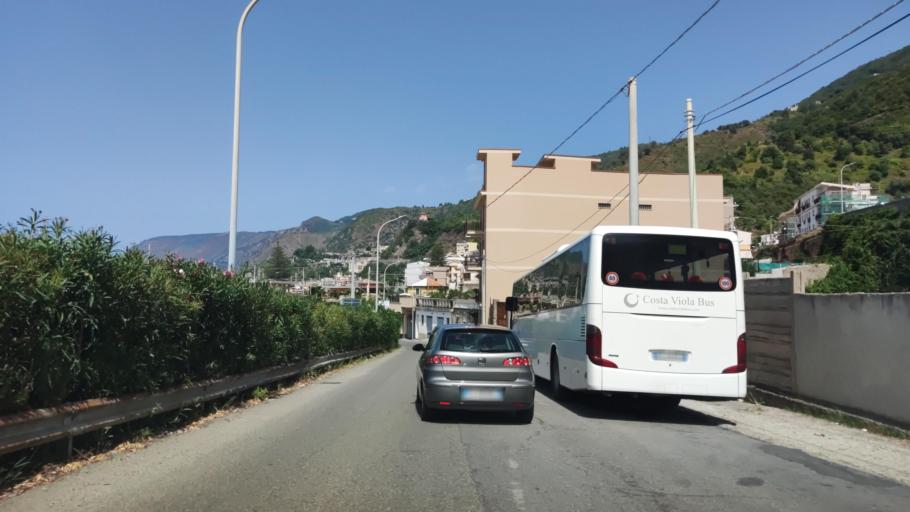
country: IT
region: Calabria
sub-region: Provincia di Reggio Calabria
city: Bagnara Calabra
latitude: 38.2810
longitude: 15.7987
